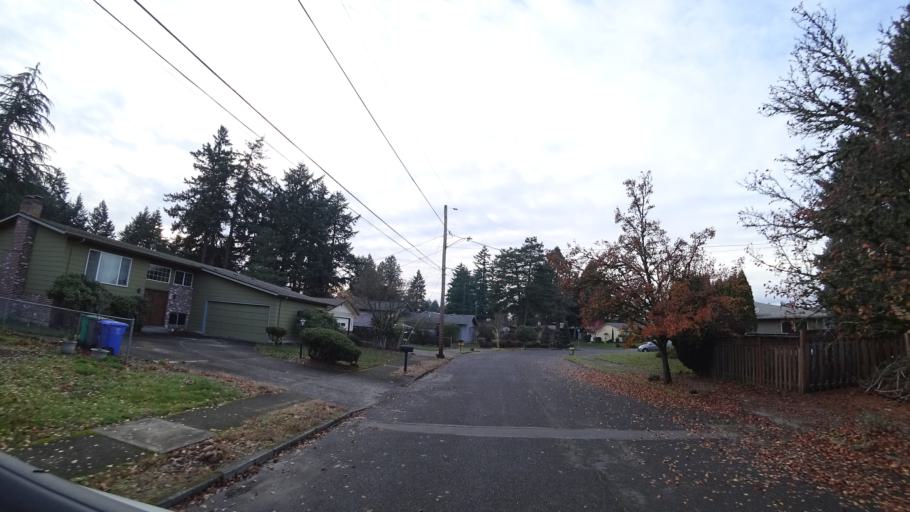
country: US
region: Oregon
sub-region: Multnomah County
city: Lents
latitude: 45.5156
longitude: -122.5225
